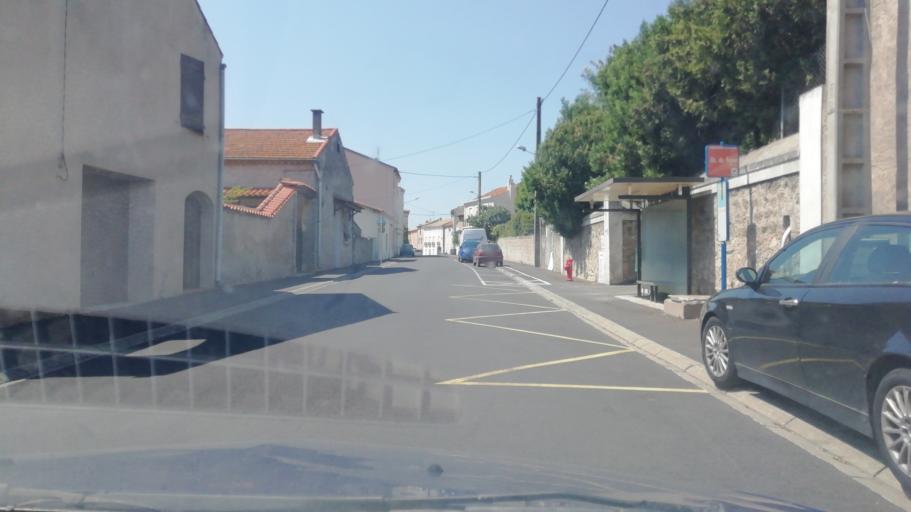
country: FR
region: Languedoc-Roussillon
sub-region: Departement de l'Herault
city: Maureilhan
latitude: 43.3574
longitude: 3.1241
